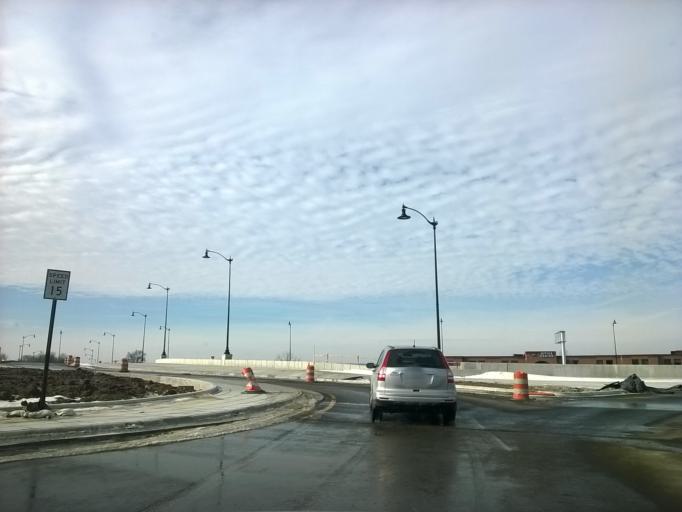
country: US
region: Indiana
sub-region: Hamilton County
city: Carmel
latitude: 39.9780
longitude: -86.1564
